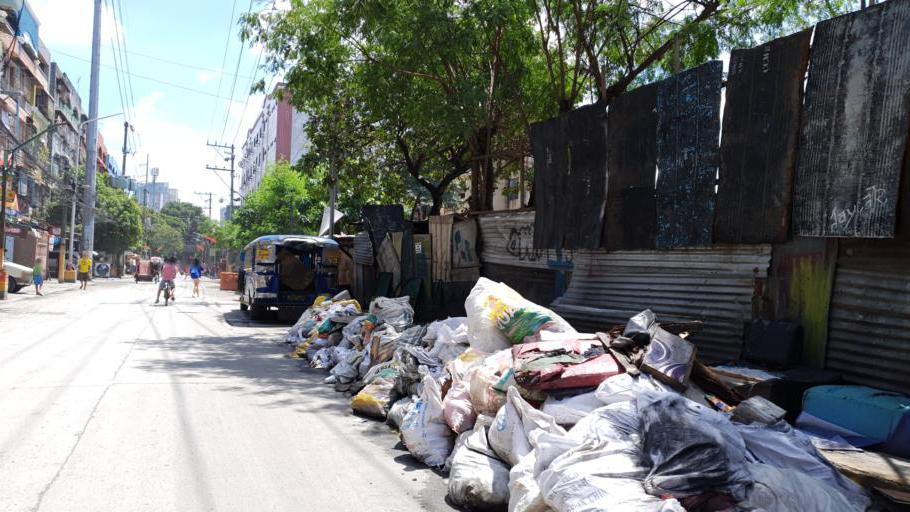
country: PH
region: Metro Manila
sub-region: City of Manila
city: Quiapo
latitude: 14.5979
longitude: 121.0031
